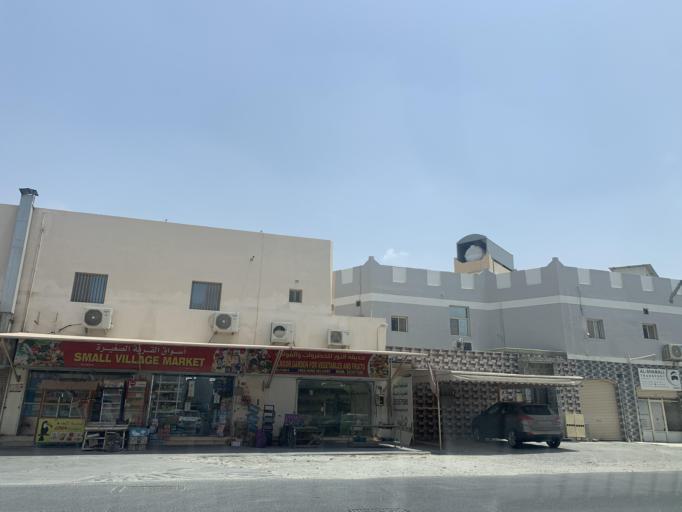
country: BH
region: Central Governorate
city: Madinat Hamad
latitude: 26.1460
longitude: 50.5012
